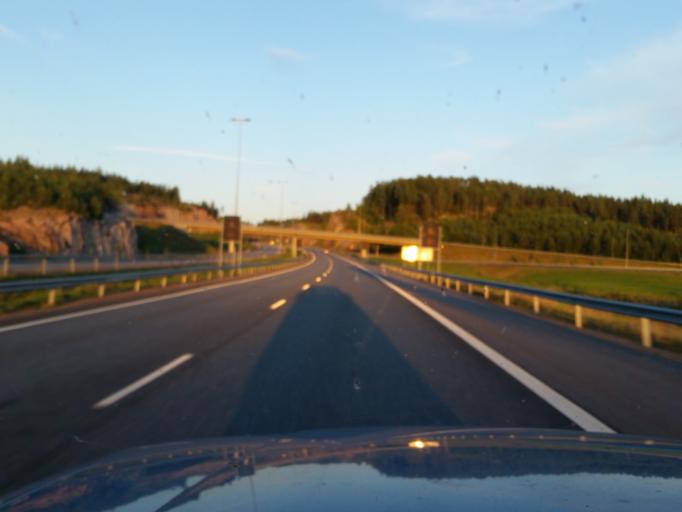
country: FI
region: Varsinais-Suomi
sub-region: Salo
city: Muurla
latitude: 60.3806
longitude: 23.3165
